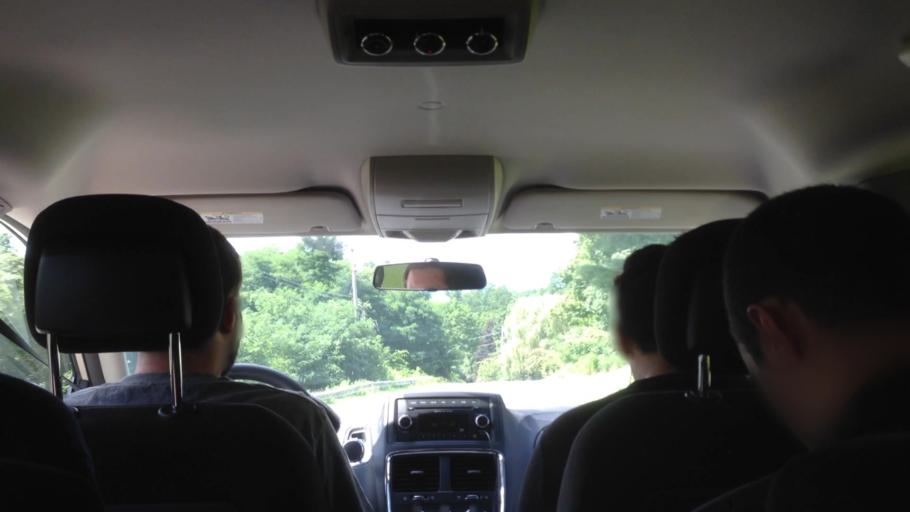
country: US
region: New York
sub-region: Dutchess County
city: Tivoli
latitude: 42.0553
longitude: -73.8916
